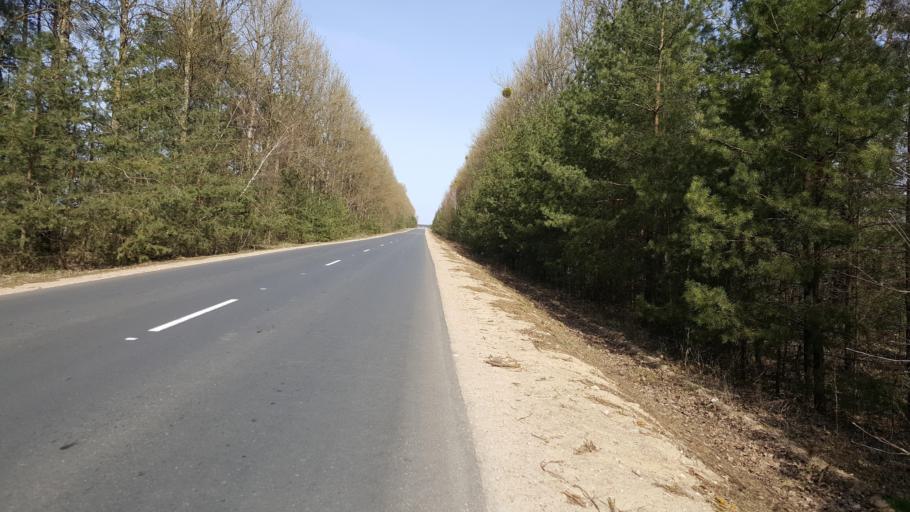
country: BY
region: Brest
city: Kamyanyets
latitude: 52.4499
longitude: 23.7374
